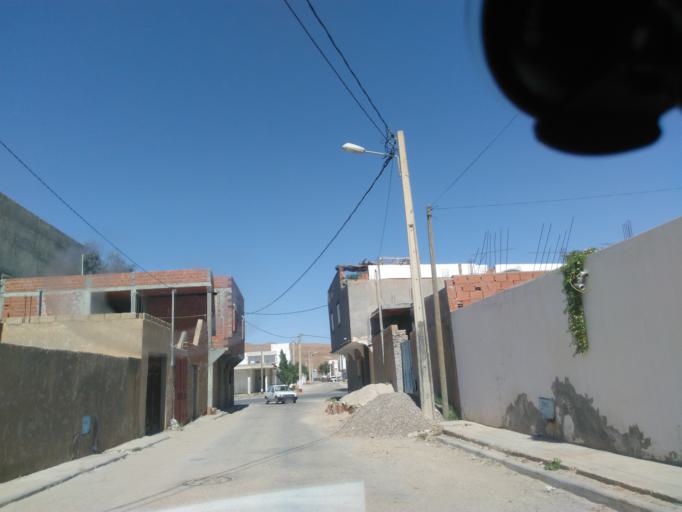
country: TN
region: Tataouine
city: Tataouine
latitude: 32.9482
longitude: 10.4655
